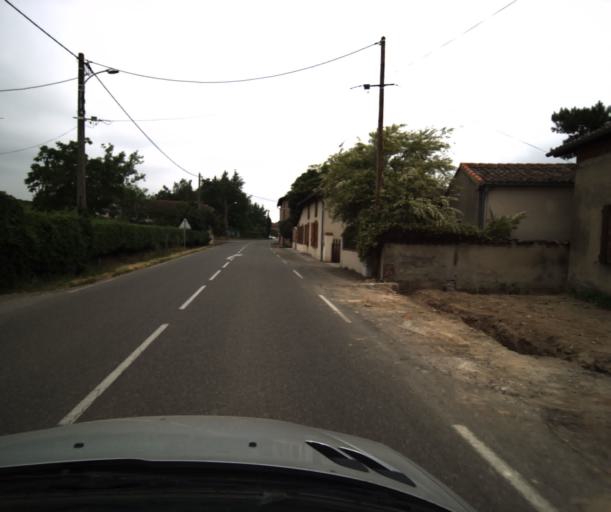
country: FR
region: Midi-Pyrenees
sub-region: Departement du Tarn-et-Garonne
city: Saint-Nicolas-de-la-Grave
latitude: 44.0606
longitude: 1.0247
